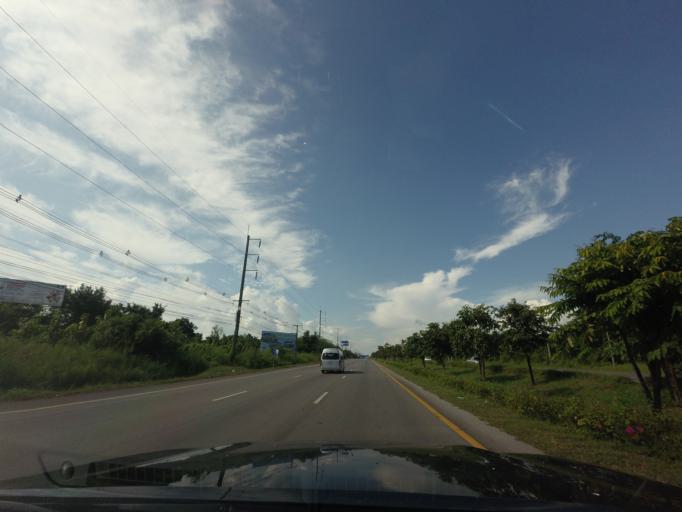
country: TH
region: Nong Khai
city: Nong Khai
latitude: 17.7929
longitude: 102.7631
